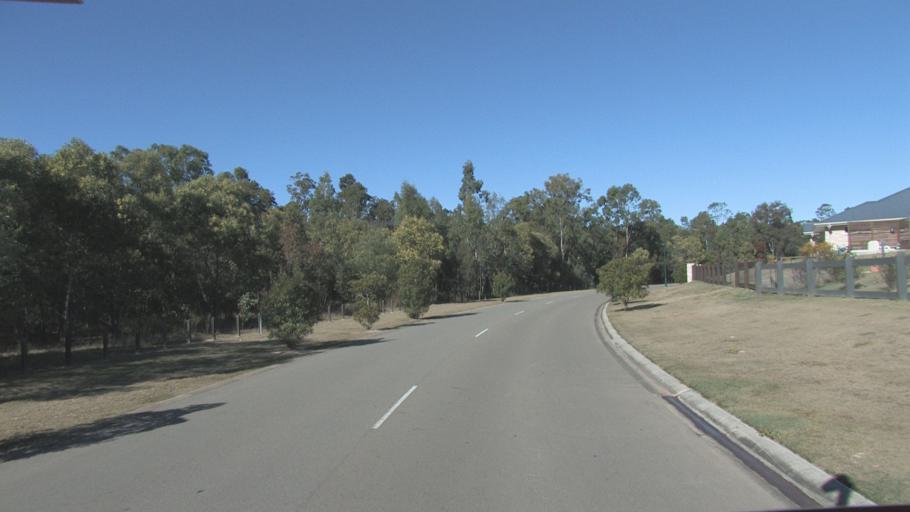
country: AU
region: Queensland
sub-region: Logan
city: North Maclean
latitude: -27.7531
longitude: 152.9664
